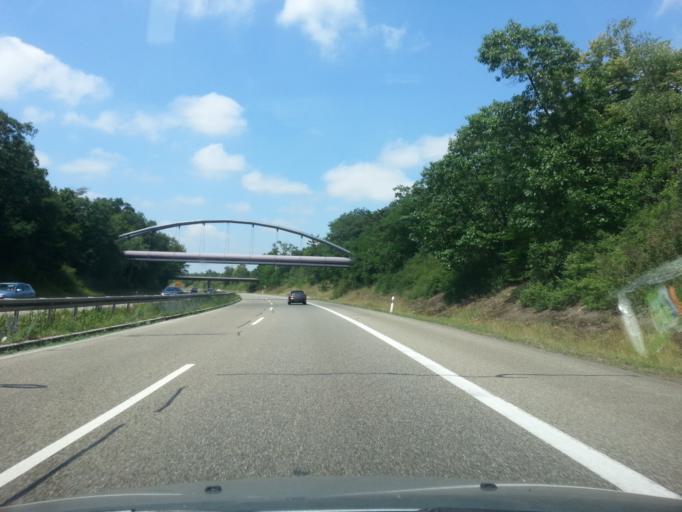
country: DE
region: Baden-Wuerttemberg
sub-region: Karlsruhe Region
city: Bruhl
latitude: 49.4329
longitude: 8.5365
